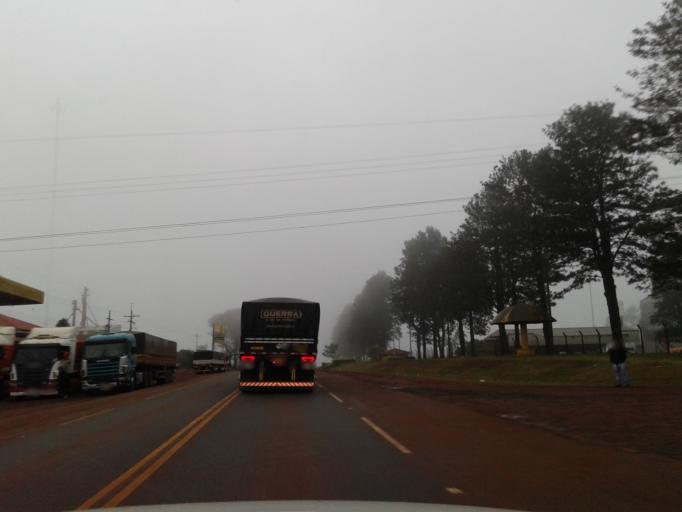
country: PY
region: Itapua
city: Pirapo
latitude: -26.8642
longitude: -55.4536
